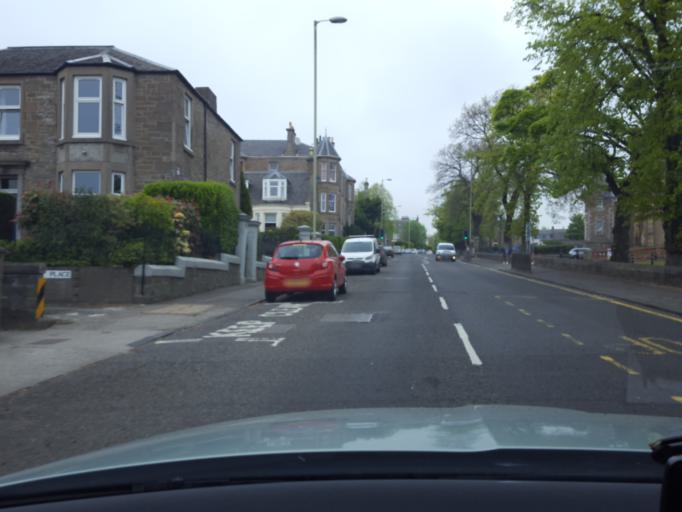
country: GB
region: Scotland
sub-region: Dundee City
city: Dundee
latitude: 56.4739
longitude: -2.9557
